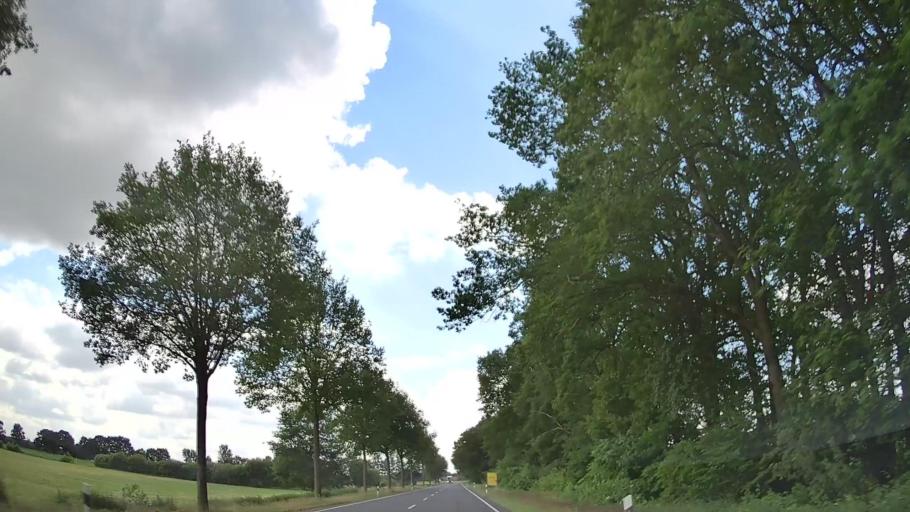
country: DE
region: Lower Saxony
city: Vechta
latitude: 52.6855
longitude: 8.3188
